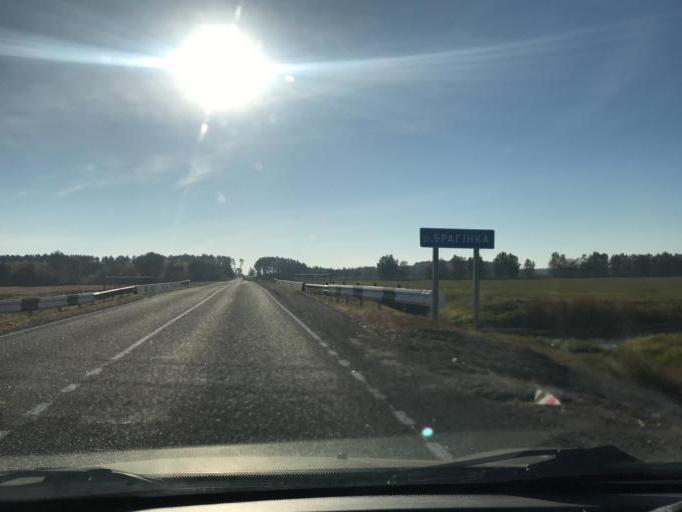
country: BY
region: Gomel
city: Brahin
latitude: 51.7727
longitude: 30.2943
